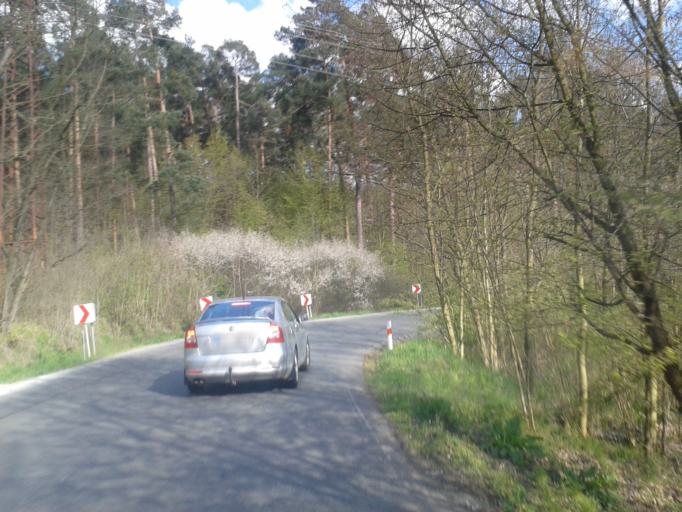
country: CZ
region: Central Bohemia
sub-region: Okres Beroun
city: Beroun
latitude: 49.9885
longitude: 14.0854
